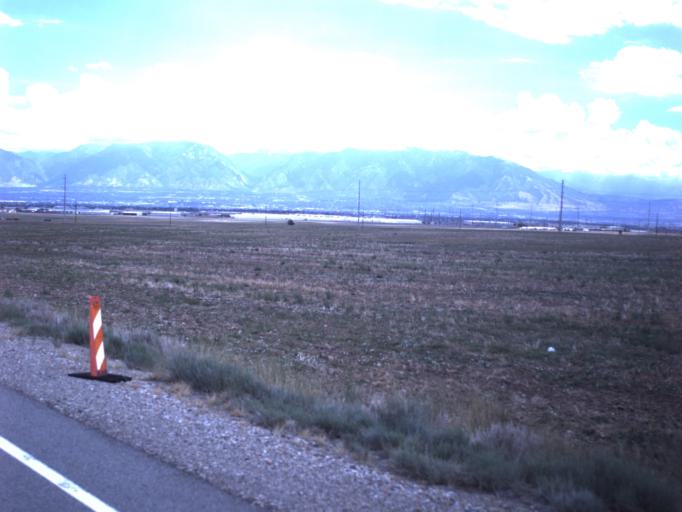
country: US
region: Utah
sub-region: Salt Lake County
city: Herriman
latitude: 40.5707
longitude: -112.0727
